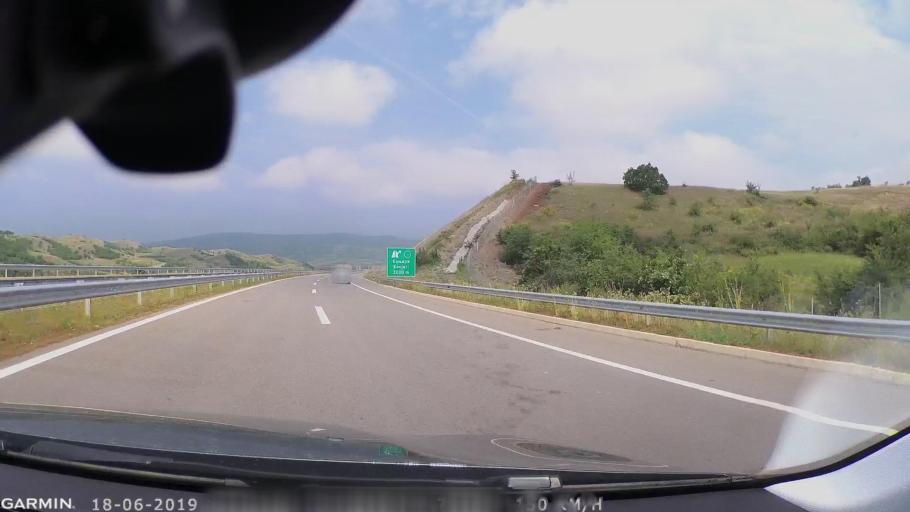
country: MK
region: Sveti Nikole
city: Gorobinci
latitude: 41.9283
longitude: 21.8309
